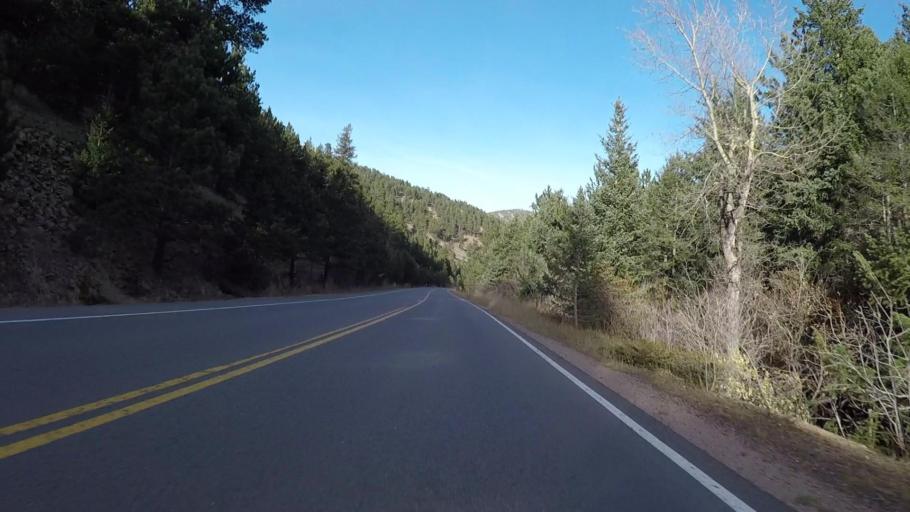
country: US
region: Colorado
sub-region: Boulder County
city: Nederland
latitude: 40.0586
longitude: -105.4904
